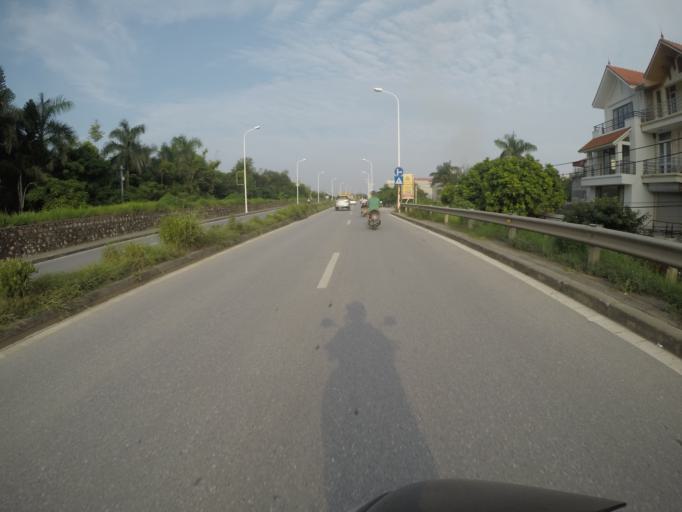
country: VN
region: Ha Noi
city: Tay Ho
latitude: 21.0893
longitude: 105.7983
